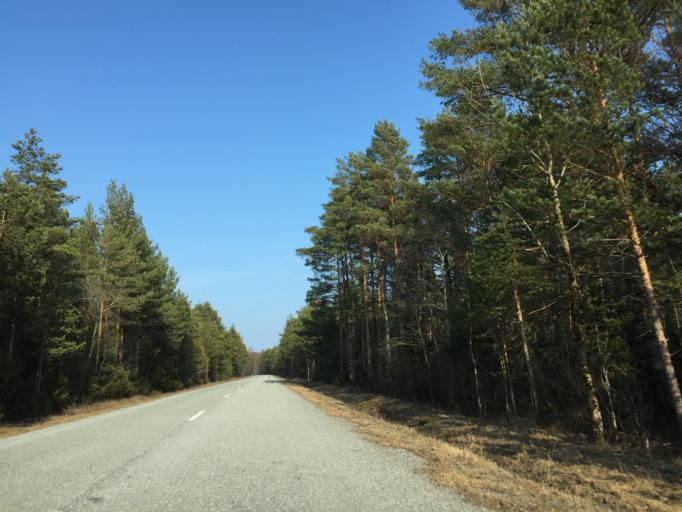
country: EE
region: Saare
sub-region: Orissaare vald
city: Orissaare
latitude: 58.5716
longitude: 23.3637
